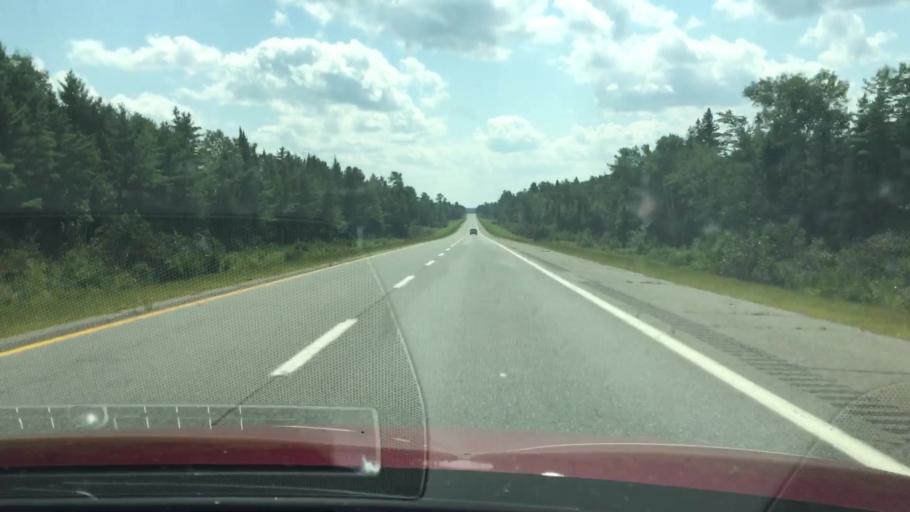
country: US
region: Maine
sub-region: Penobscot County
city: Lincoln
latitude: 45.4067
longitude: -68.5969
